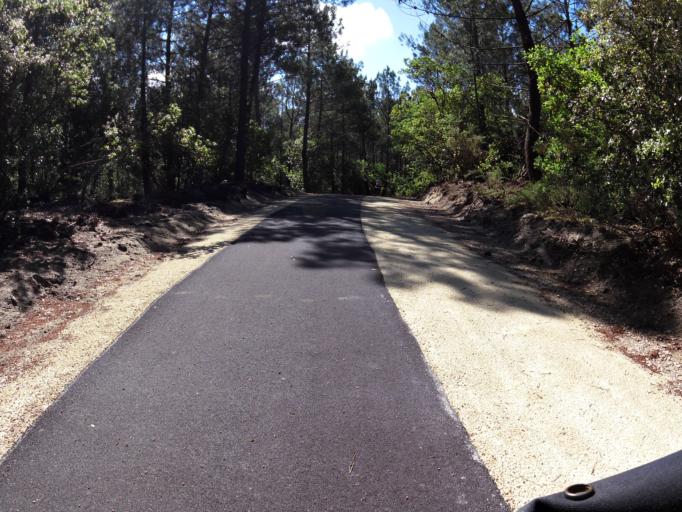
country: FR
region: Aquitaine
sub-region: Departement de la Gironde
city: Lacanau
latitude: 45.0309
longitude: -1.1608
